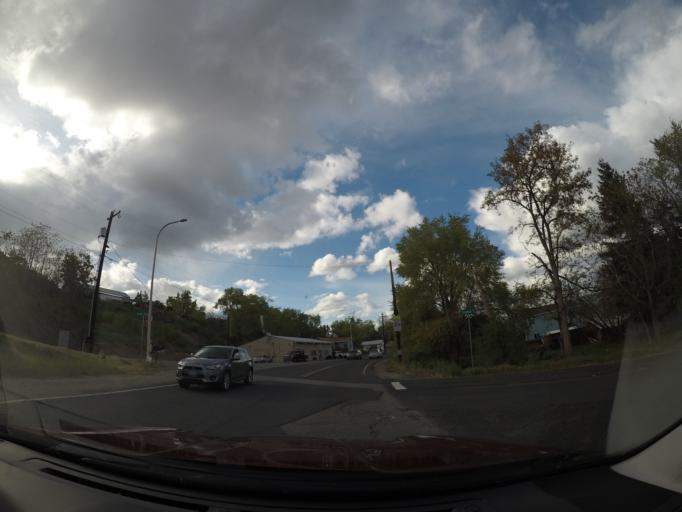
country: US
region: Washington
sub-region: Chelan County
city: South Wenatchee
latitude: 47.3967
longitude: -120.3027
